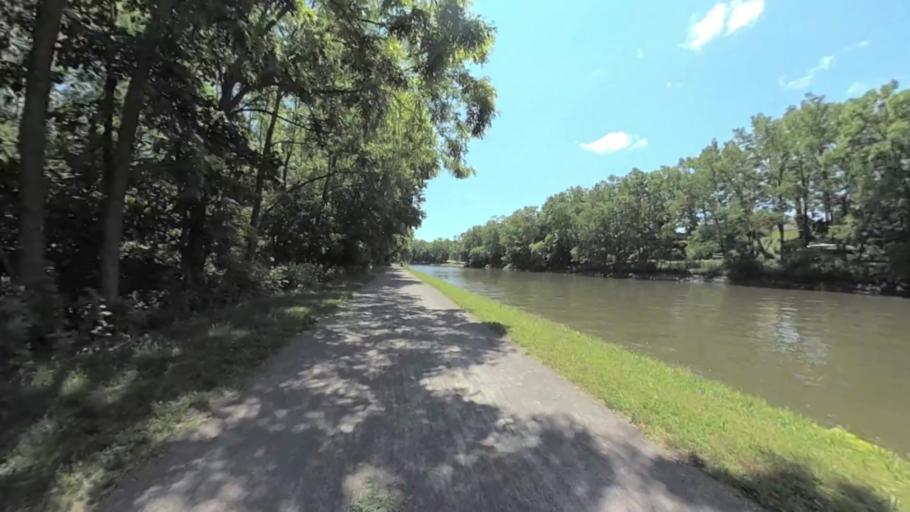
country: US
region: New York
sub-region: Monroe County
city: Pittsford
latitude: 43.0644
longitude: -77.4849
